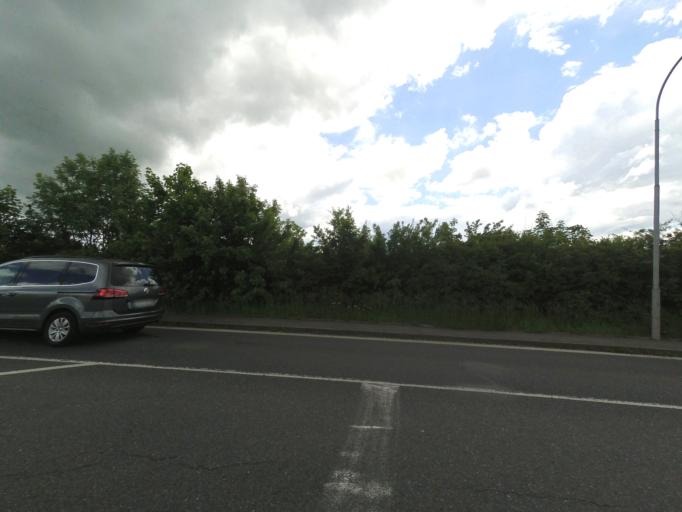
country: CZ
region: Plzensky
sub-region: Okres Domazlice
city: Kdyne
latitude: 49.3919
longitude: 13.0294
